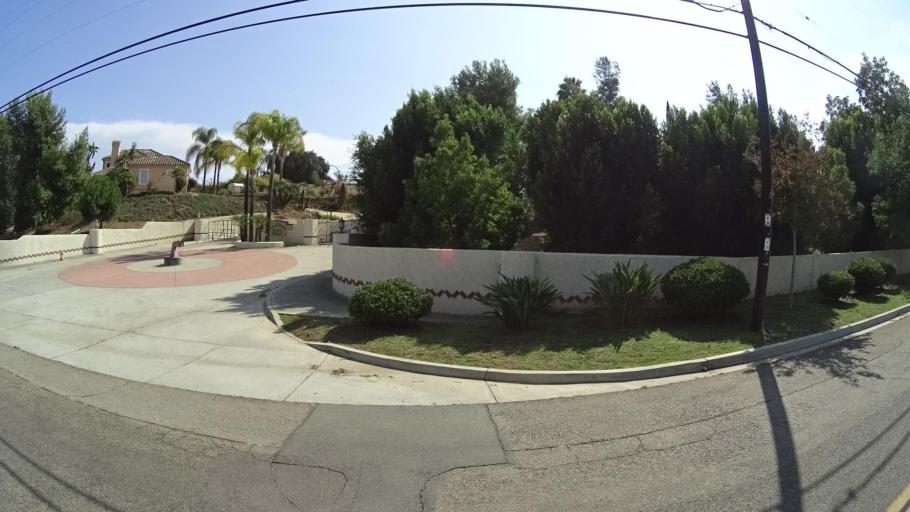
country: US
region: California
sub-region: San Diego County
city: Escondido
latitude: 33.1047
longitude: -117.0568
